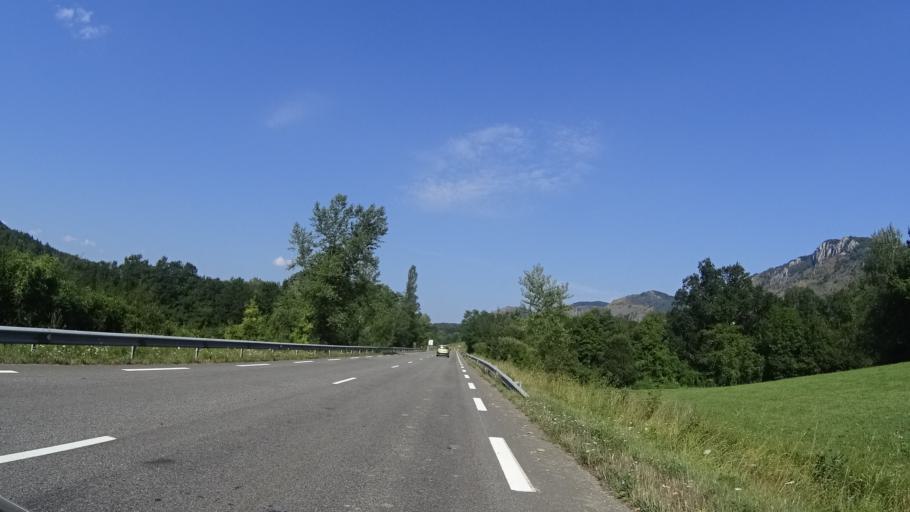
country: FR
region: Midi-Pyrenees
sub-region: Departement de l'Ariege
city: Saint-Paul-de-Jarrat
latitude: 42.9333
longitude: 1.7194
